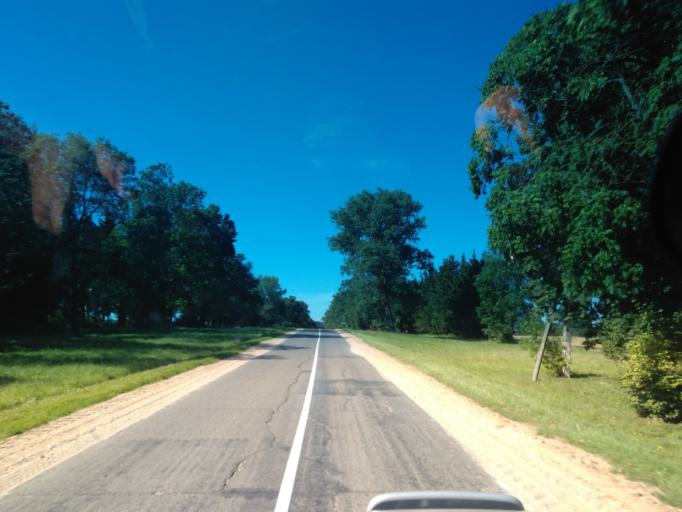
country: BY
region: Minsk
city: Stan'kava
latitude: 53.6349
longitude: 27.2798
